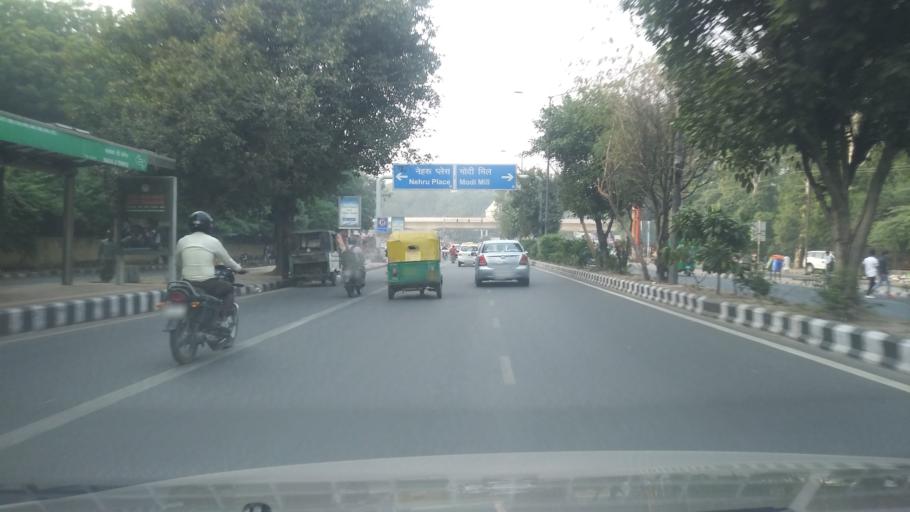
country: IN
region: Uttar Pradesh
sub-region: Gautam Buddha Nagar
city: Noida
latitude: 28.5476
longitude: 77.2629
